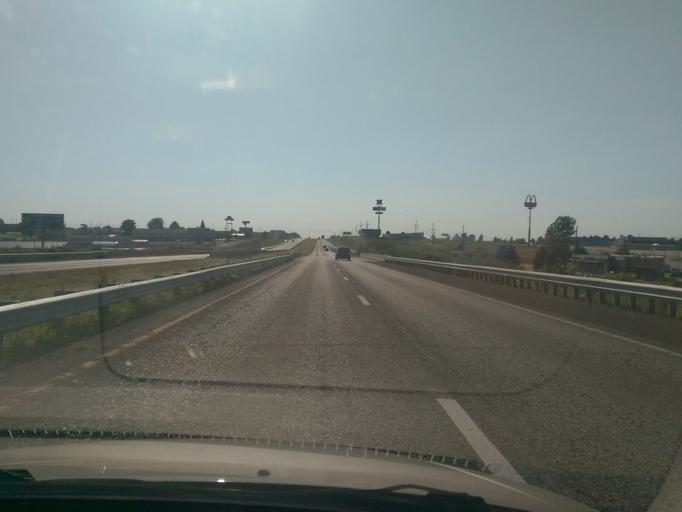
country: US
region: Missouri
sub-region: Lafayette County
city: Concordia
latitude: 38.9919
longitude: -93.5666
